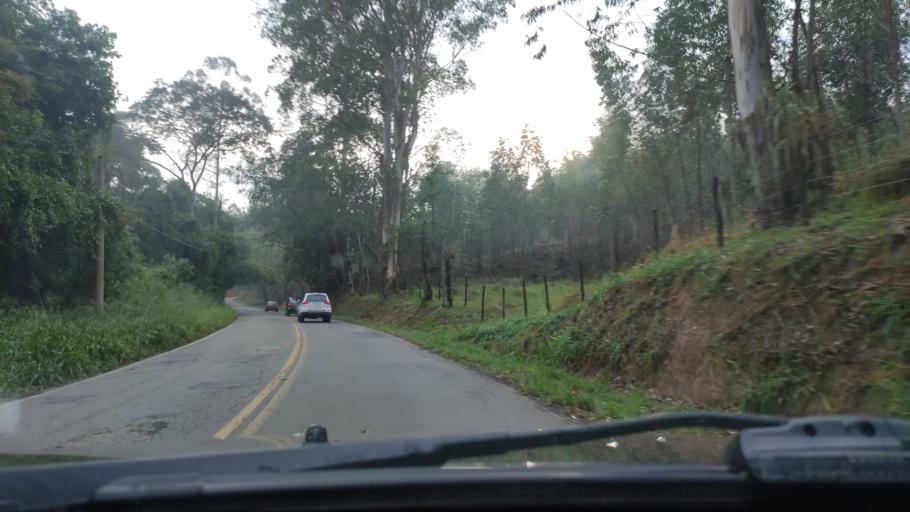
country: BR
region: Sao Paulo
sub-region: Jarinu
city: Jarinu
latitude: -23.1326
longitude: -46.7761
